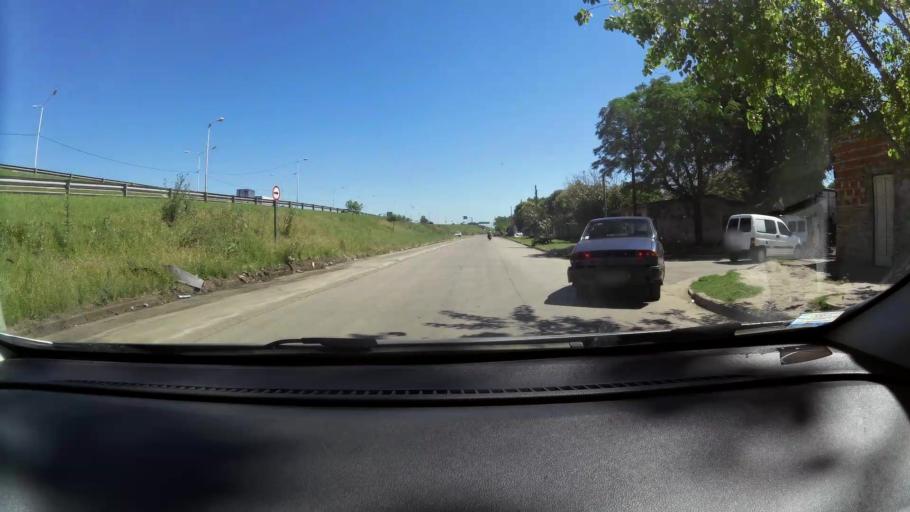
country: AR
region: Santa Fe
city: Perez
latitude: -32.9579
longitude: -60.7208
